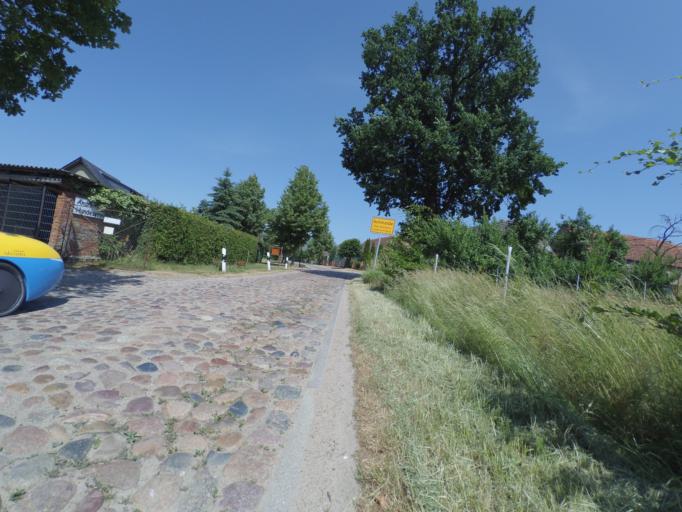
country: DE
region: Brandenburg
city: Gerdshagen
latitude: 53.2782
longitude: 12.2830
